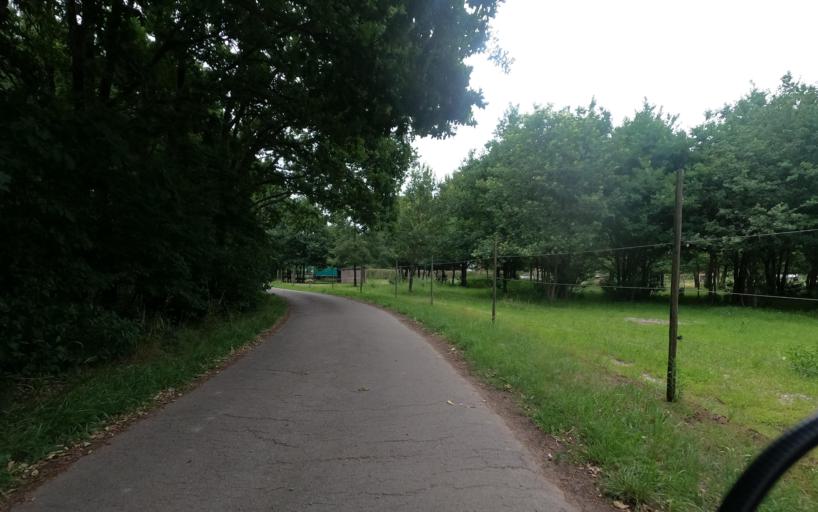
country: BE
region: Flanders
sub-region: Provincie Vlaams-Brabant
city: Rotselaar
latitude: 50.9771
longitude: 4.7433
